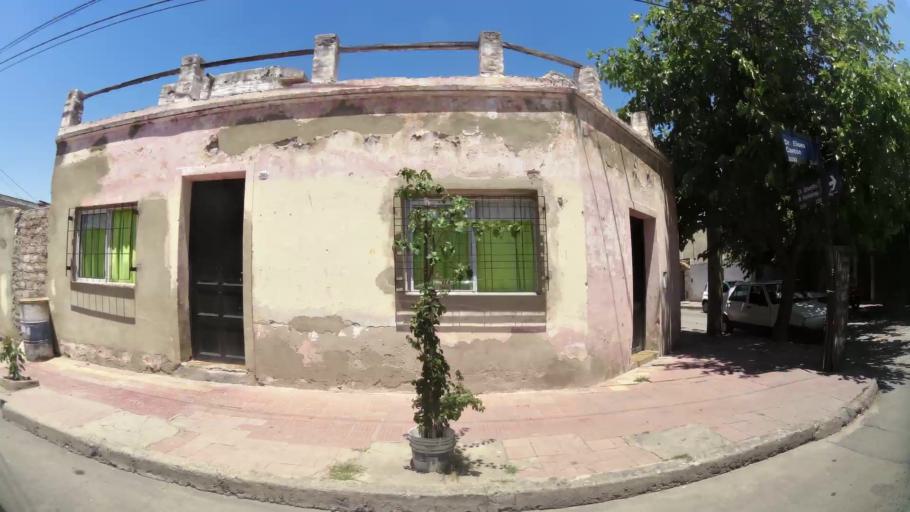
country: AR
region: Cordoba
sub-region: Departamento de Capital
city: Cordoba
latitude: -31.3955
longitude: -64.2061
